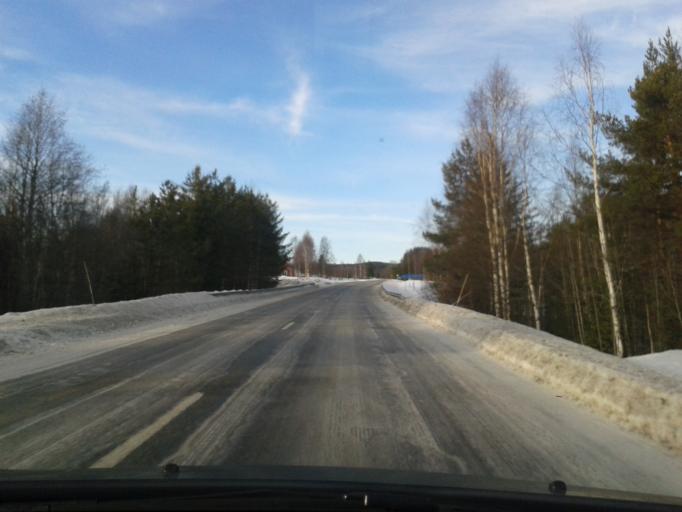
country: SE
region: Vaesternorrland
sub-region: OErnskoeldsviks Kommun
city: Bredbyn
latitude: 63.5650
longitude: 17.9341
